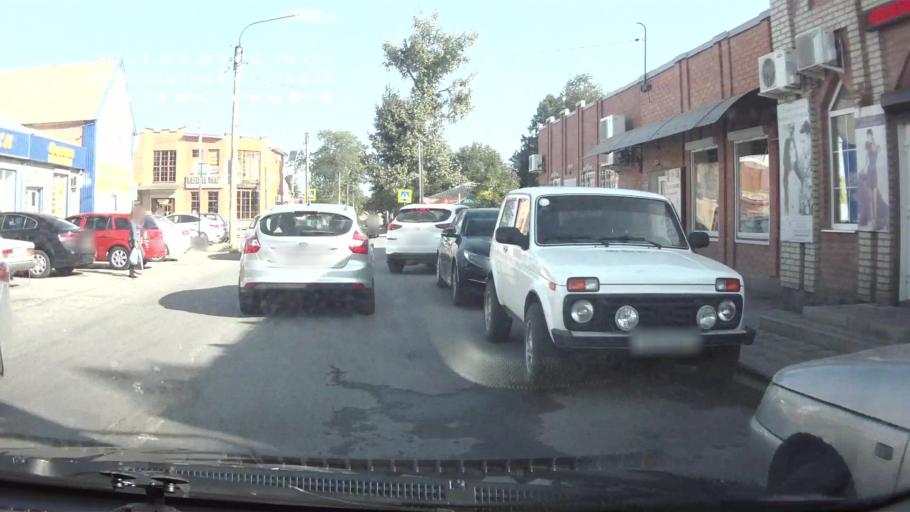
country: RU
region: Rostov
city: Tselina
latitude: 46.5368
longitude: 41.0270
